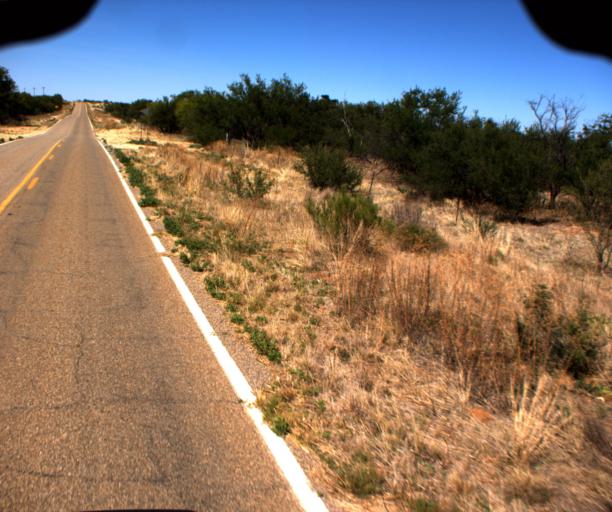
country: US
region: Arizona
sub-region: Santa Cruz County
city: Tubac
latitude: 31.5135
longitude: -111.5442
